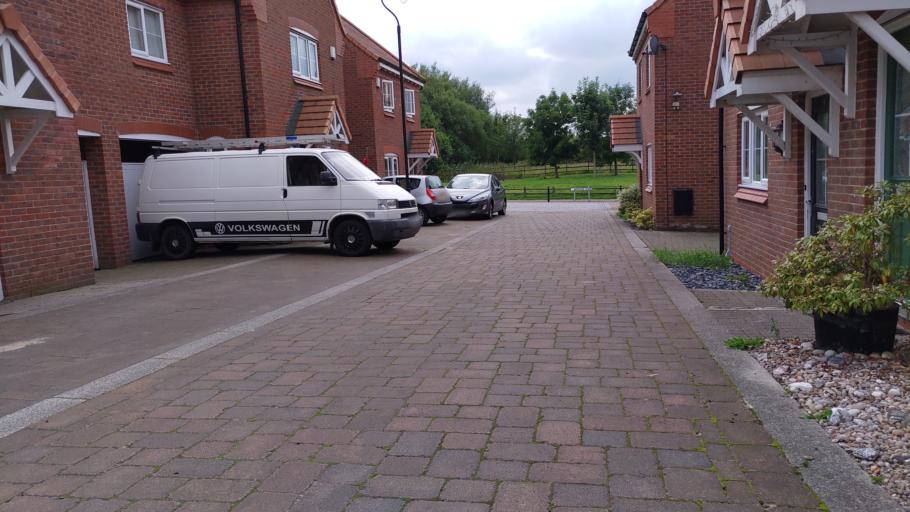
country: GB
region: England
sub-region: Lancashire
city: Coppull
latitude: 53.6302
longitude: -2.6381
